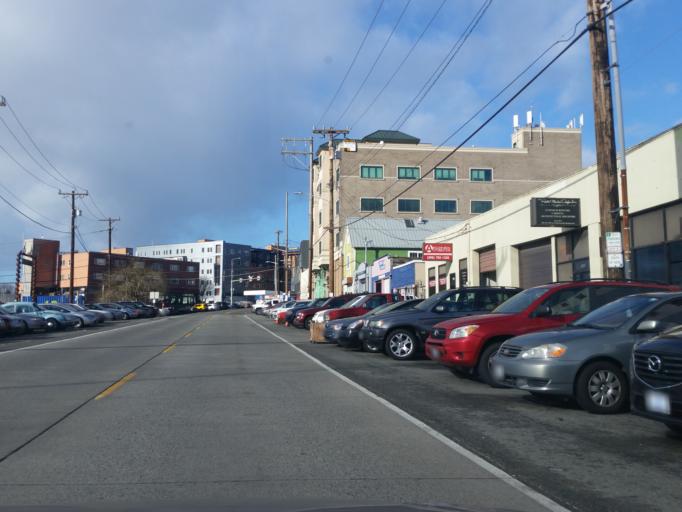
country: US
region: Washington
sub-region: King County
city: Seattle
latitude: 47.6675
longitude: -122.3862
